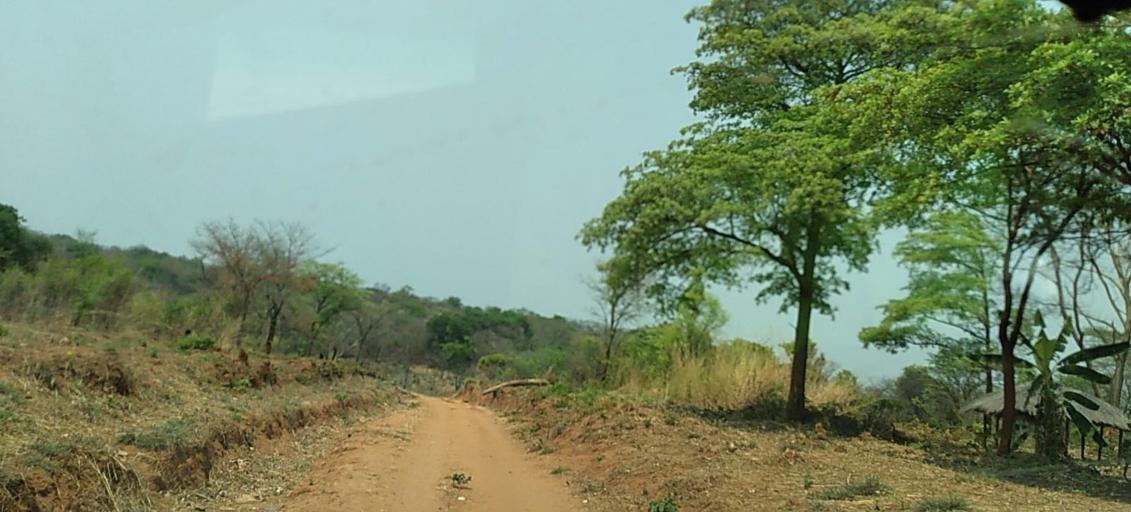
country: ZM
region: Western
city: Lukulu
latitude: -13.9815
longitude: 23.2282
